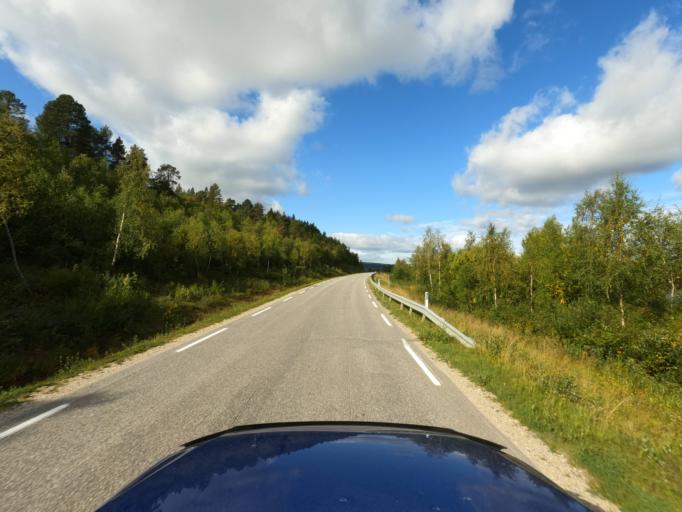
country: NO
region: Finnmark Fylke
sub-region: Karasjok
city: Karasjohka
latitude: 69.4499
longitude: 25.5863
